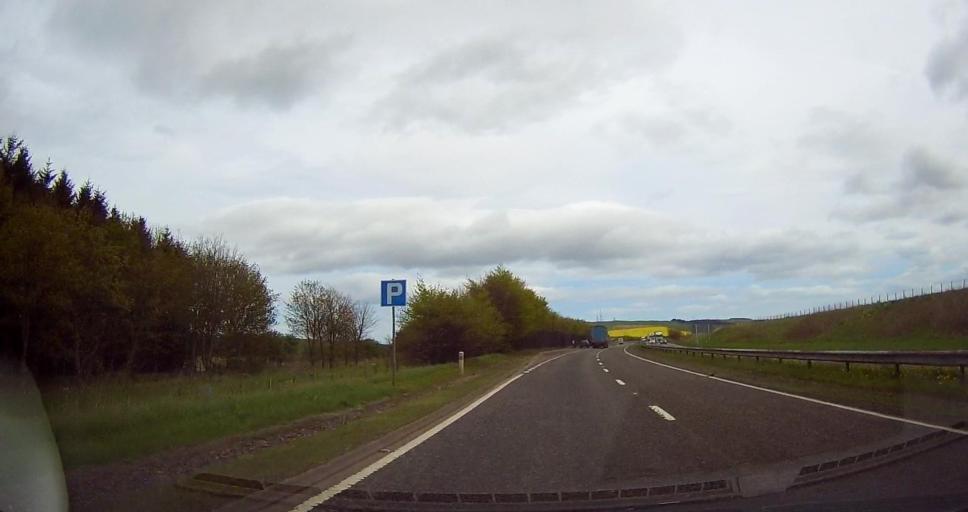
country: GB
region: Scotland
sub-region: Aberdeenshire
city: Inverbervie
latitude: 56.9098
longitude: -2.3519
